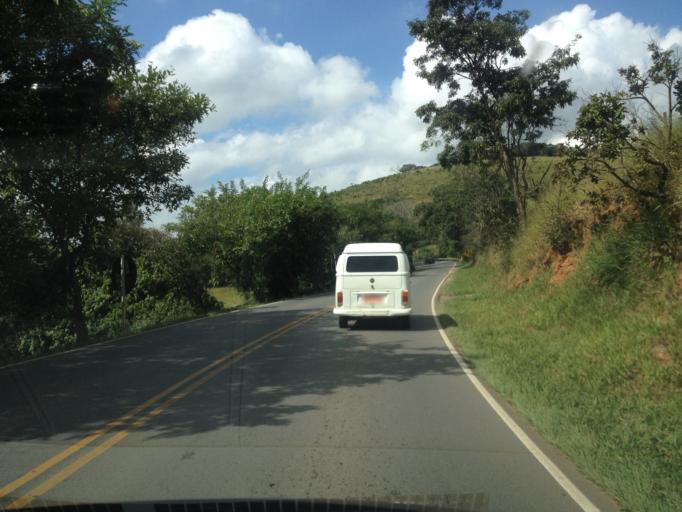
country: BR
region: Minas Gerais
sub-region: Itanhandu
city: Itanhandu
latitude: -22.2034
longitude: -44.9632
